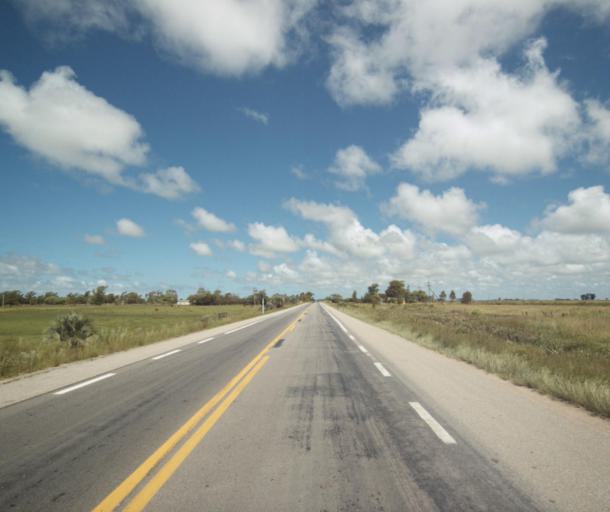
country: BR
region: Rio Grande do Sul
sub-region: Arroio Grande
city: Arroio Grande
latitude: -32.8544
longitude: -52.7042
